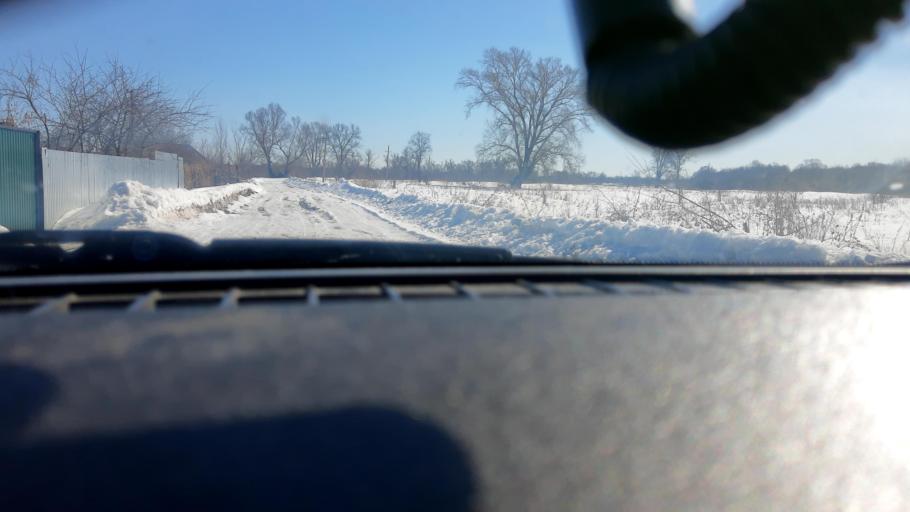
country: RU
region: Bashkortostan
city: Ufa
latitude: 54.7763
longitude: 56.1910
